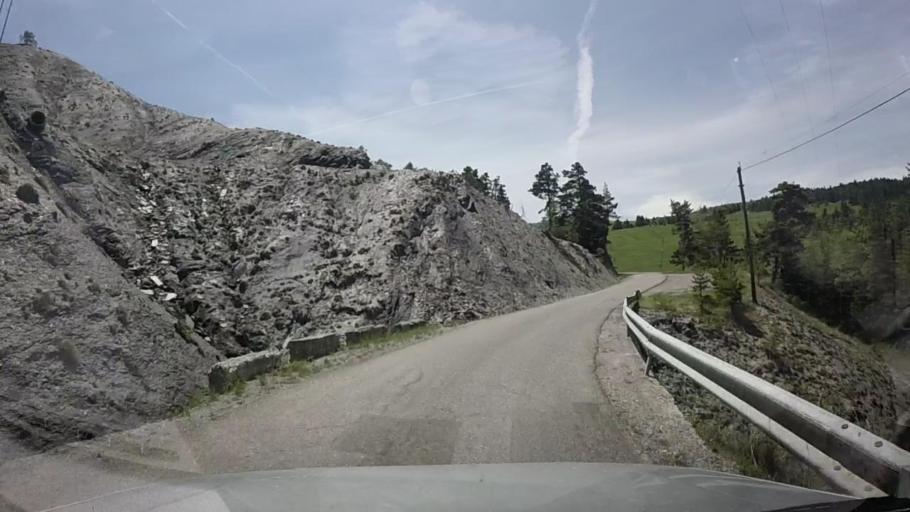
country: FR
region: Provence-Alpes-Cote d'Azur
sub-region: Departement des Alpes-de-Haute-Provence
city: Seyne-les-Alpes
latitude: 44.3289
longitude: 6.3278
